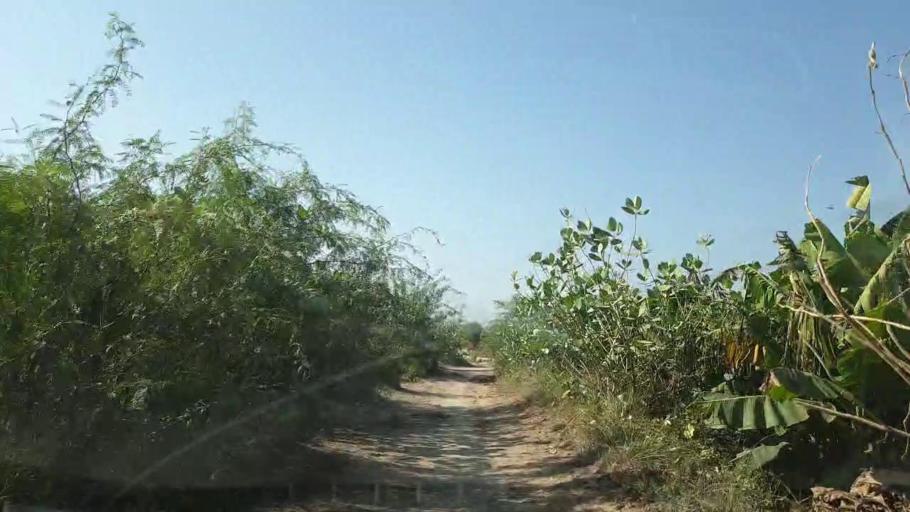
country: PK
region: Sindh
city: Tando Jam
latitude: 25.3270
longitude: 68.5935
